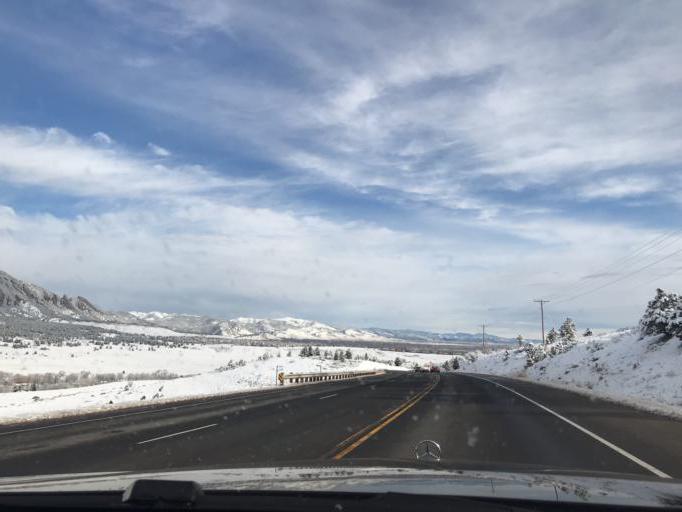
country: US
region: Colorado
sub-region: Boulder County
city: Superior
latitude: 39.9426
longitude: -105.2357
